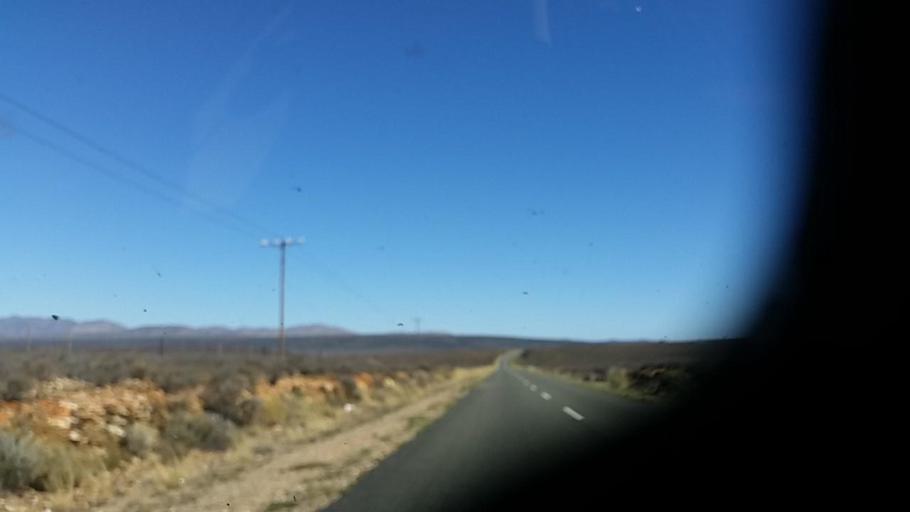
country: ZA
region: Eastern Cape
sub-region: Cacadu District Municipality
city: Willowmore
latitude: -33.5247
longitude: 23.1086
